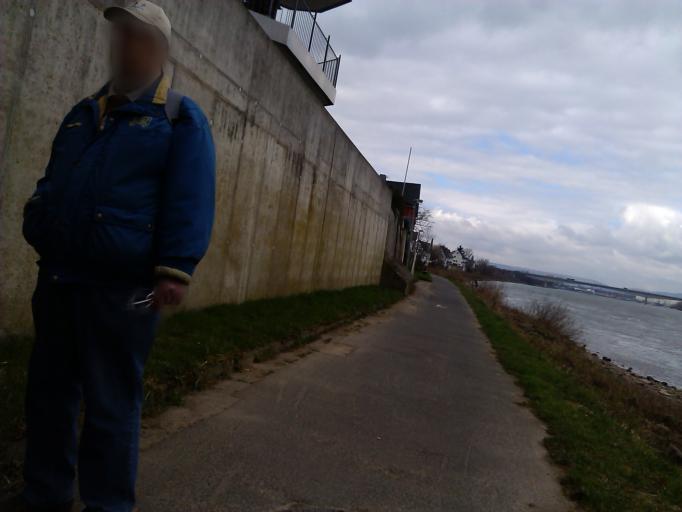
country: DE
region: Rheinland-Pfalz
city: Weitersburg
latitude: 50.3982
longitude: 7.5869
